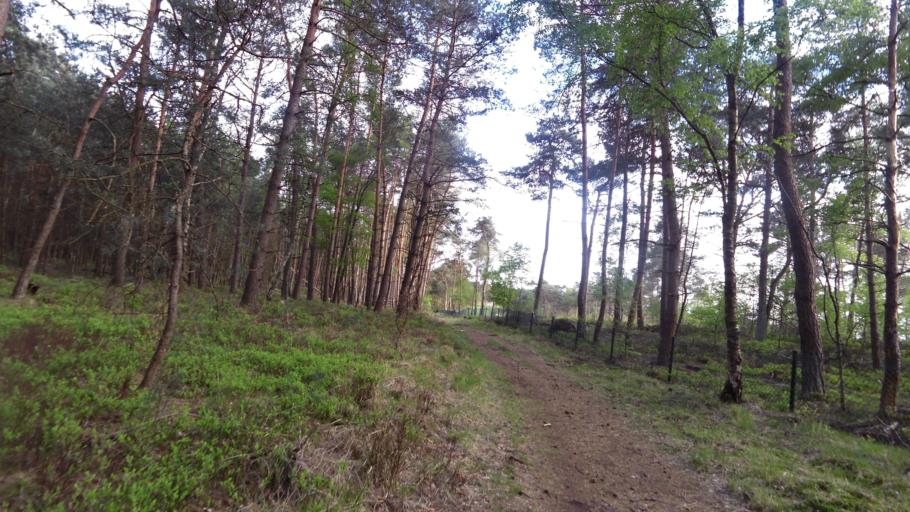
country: NL
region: Gelderland
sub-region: Gemeente Rozendaal
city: Rozendaal
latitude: 52.0271
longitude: 5.9393
